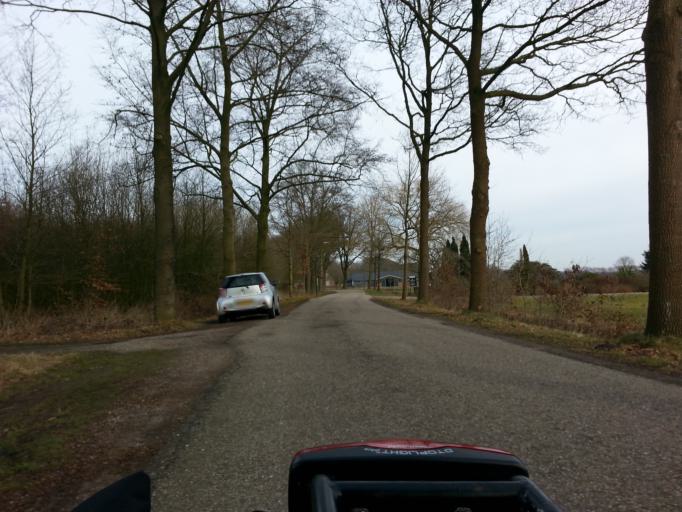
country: NL
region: Utrecht
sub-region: Gemeente Woudenberg
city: Woudenberg
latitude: 52.0935
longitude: 5.3887
